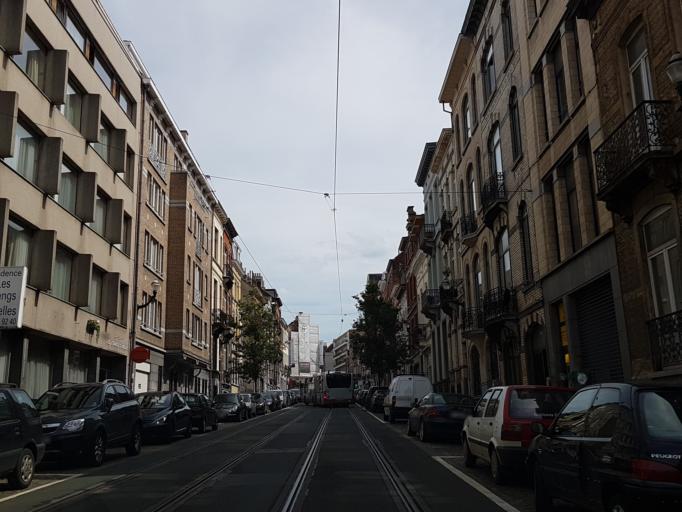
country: BE
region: Brussels Capital
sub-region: Bruxelles-Capitale
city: Brussels
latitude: 50.8217
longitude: 4.3758
